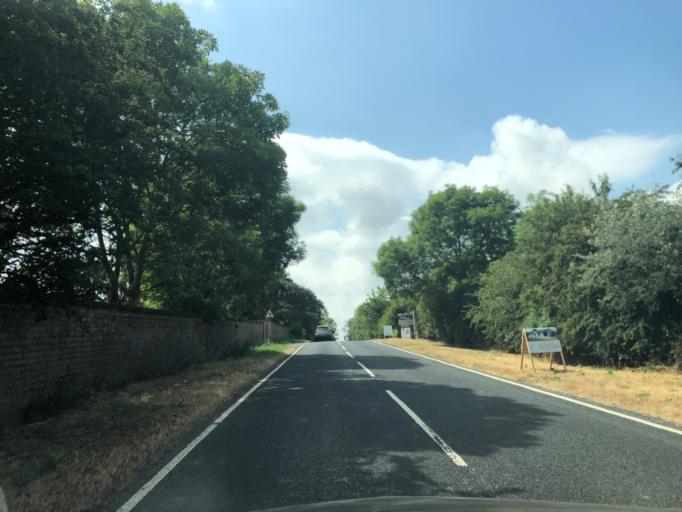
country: GB
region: England
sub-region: North Yorkshire
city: Stokesley
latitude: 54.4577
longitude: -1.2651
